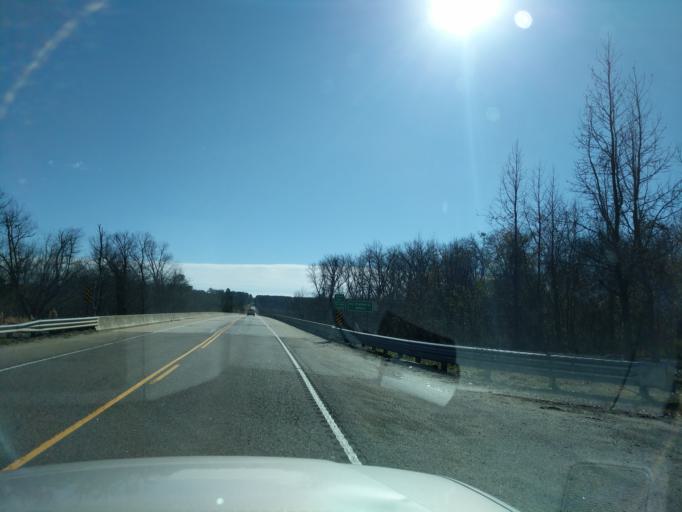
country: US
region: South Carolina
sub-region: Greenwood County
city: Ninety Six
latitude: 34.1766
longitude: -81.8660
